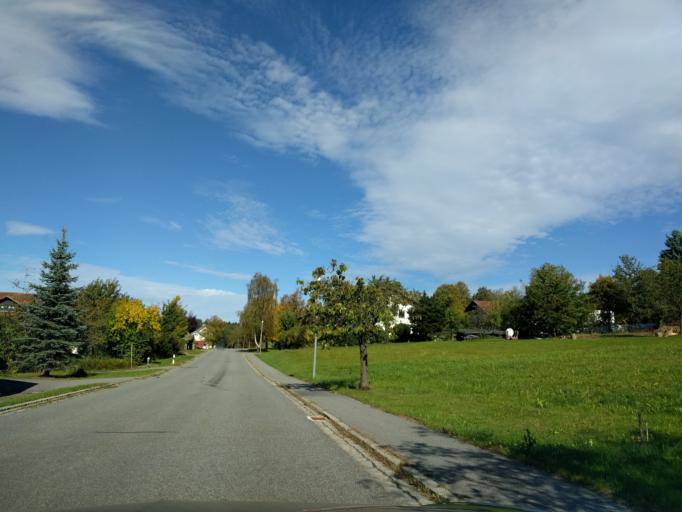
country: DE
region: Bavaria
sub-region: Upper Palatinate
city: Kotzting
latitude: 49.1411
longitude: 12.8883
